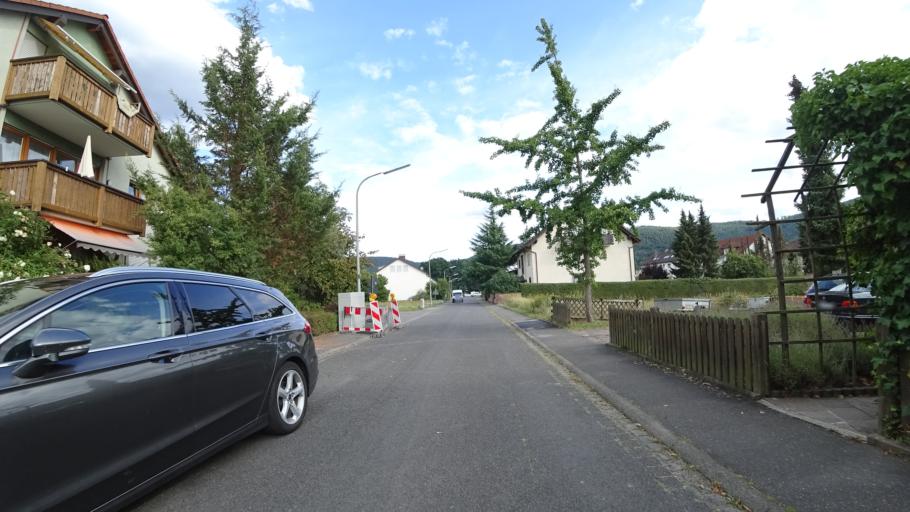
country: DE
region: Bavaria
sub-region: Regierungsbezirk Unterfranken
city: Miltenberg
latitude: 49.7107
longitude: 9.2509
